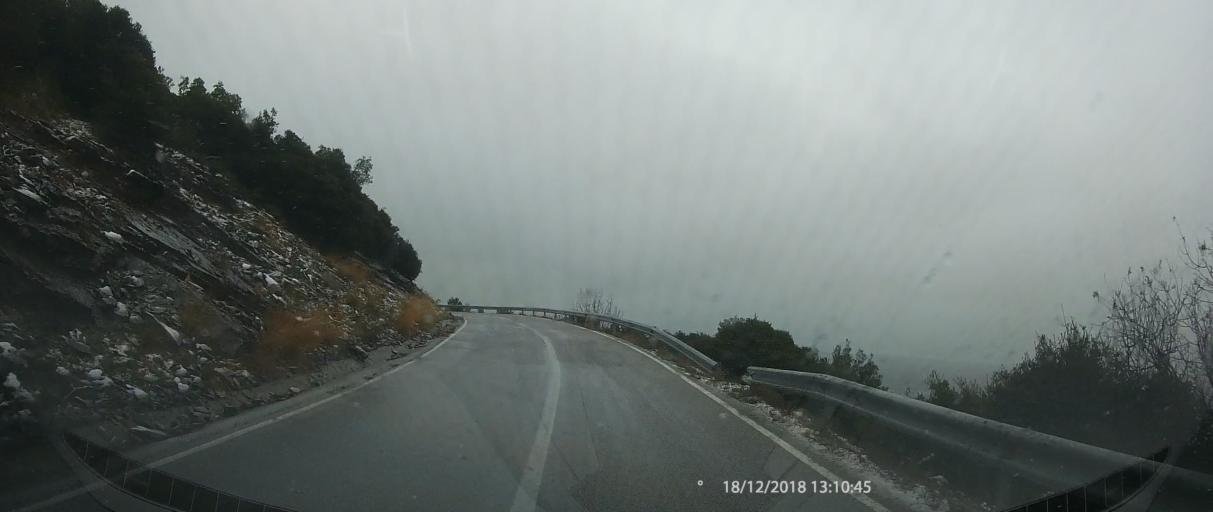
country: GR
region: Central Macedonia
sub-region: Nomos Pierias
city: Litochoro
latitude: 40.1085
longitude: 22.4794
